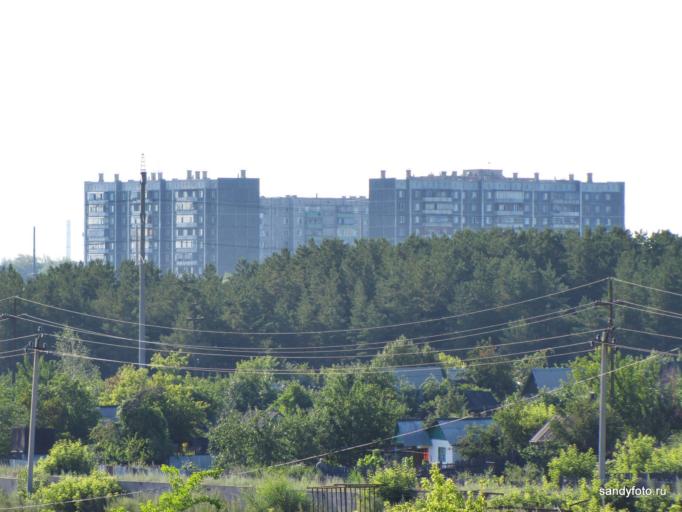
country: RU
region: Chelyabinsk
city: Bobrovka
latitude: 54.0404
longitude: 61.6587
